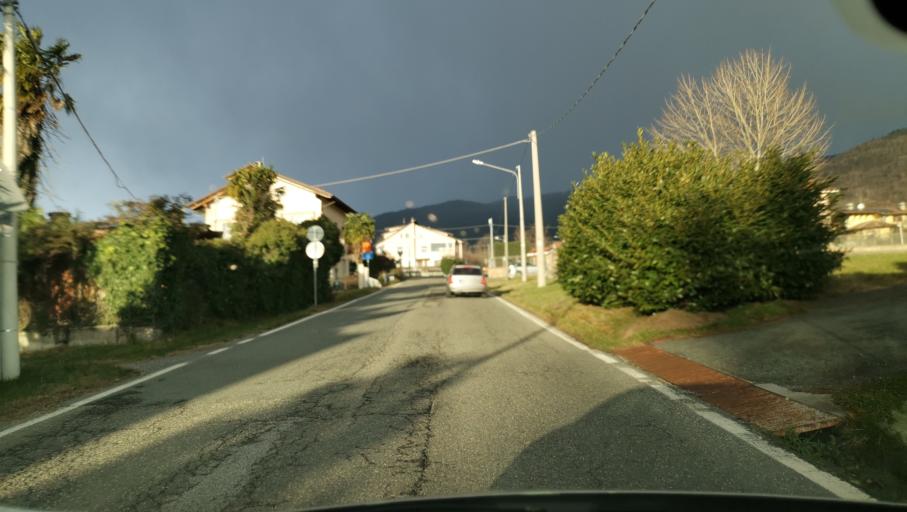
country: IT
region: Piedmont
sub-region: Provincia di Torino
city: Coazze
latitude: 45.0517
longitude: 7.3229
